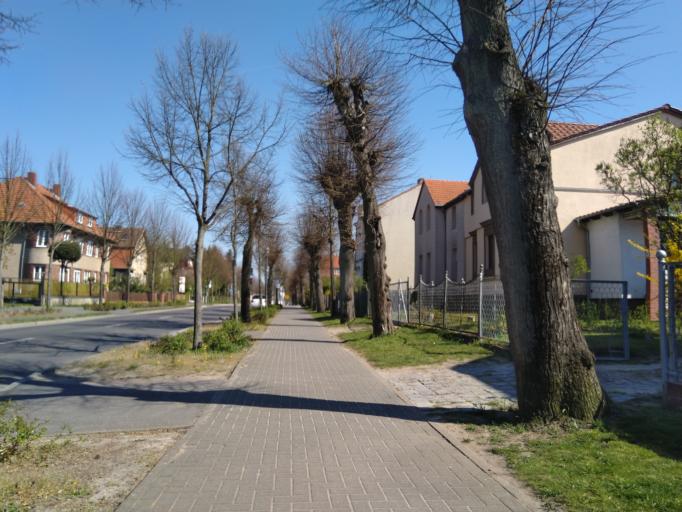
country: DE
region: Brandenburg
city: Biesenthal
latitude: 52.7665
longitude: 13.6390
